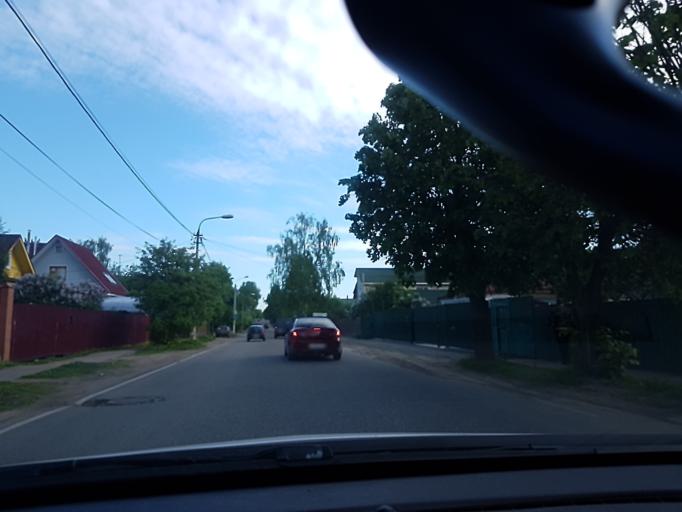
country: RU
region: Moskovskaya
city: Istra
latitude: 55.9165
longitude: 36.8680
